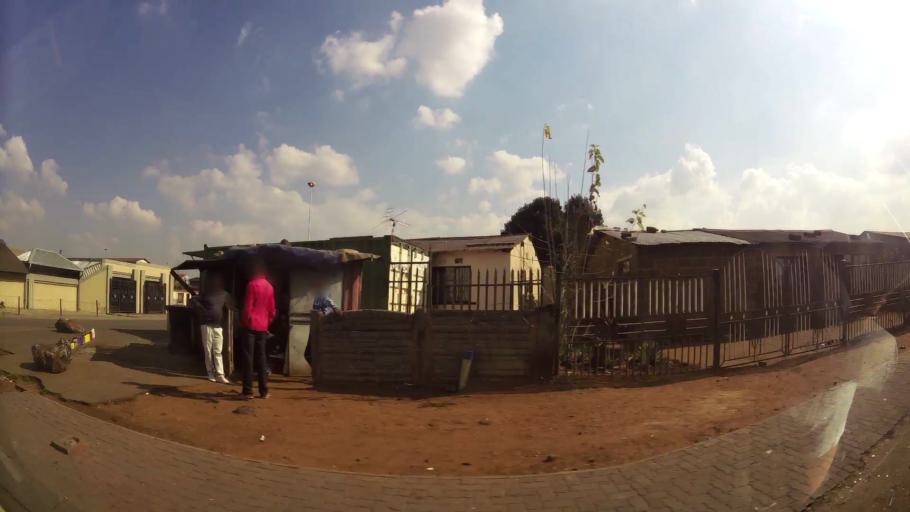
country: ZA
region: Gauteng
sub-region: Ekurhuleni Metropolitan Municipality
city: Germiston
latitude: -26.3353
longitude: 28.1496
